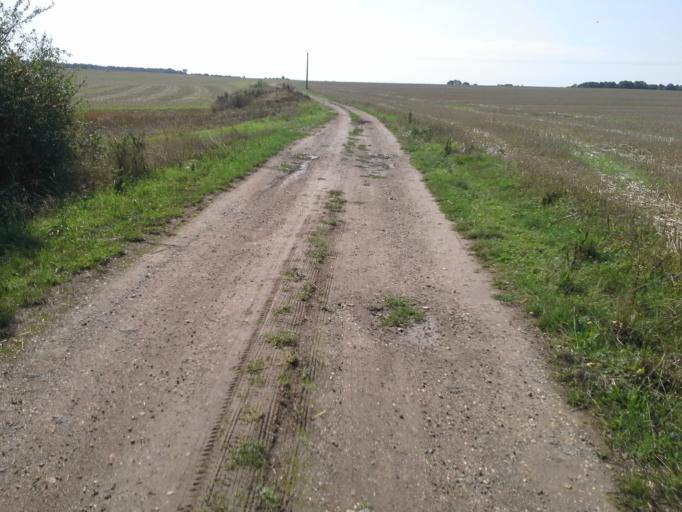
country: FR
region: Centre
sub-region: Departement du Loir-et-Cher
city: Villiers-sur-Loir
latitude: 47.8231
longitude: 0.9881
